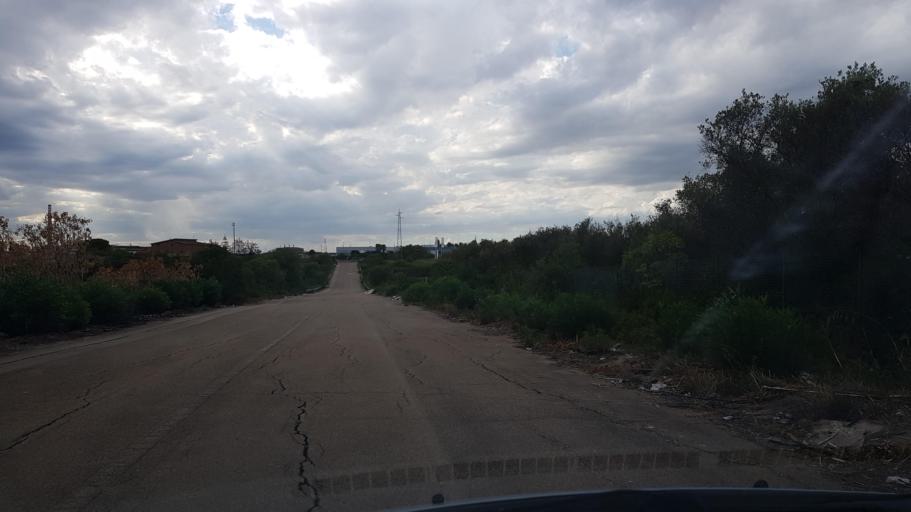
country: IT
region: Apulia
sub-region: Provincia di Taranto
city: Paolo VI
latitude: 40.5133
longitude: 17.2571
